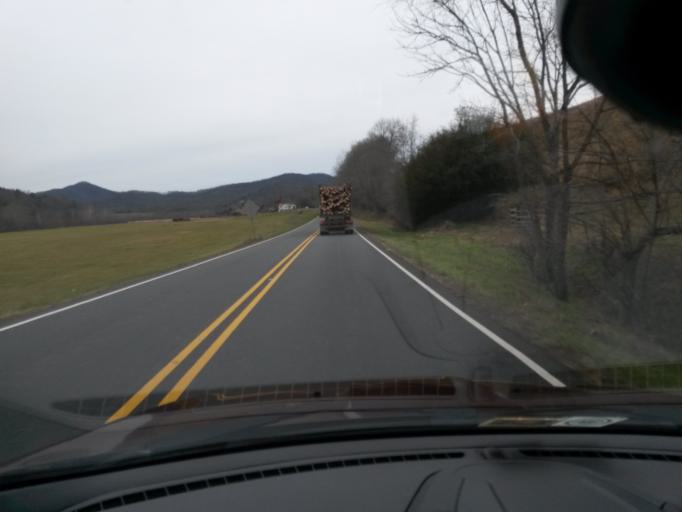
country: US
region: Virginia
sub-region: Amherst County
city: Amherst
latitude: 37.6652
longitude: -79.1844
